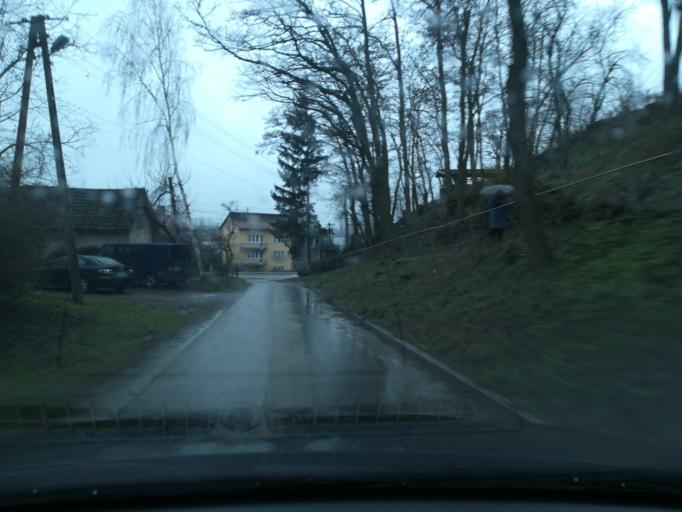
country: PL
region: Subcarpathian Voivodeship
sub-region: Powiat lancucki
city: Kosina
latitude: 50.0690
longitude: 22.3336
